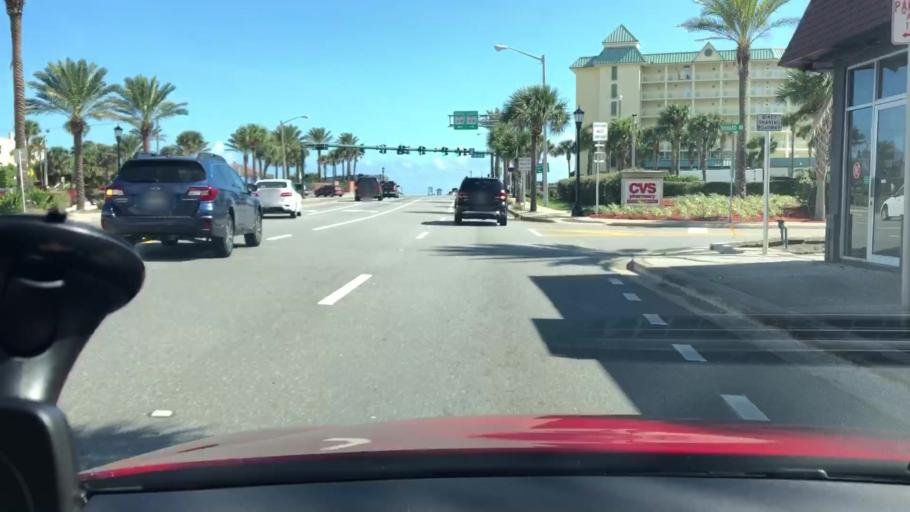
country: US
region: Florida
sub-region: Volusia County
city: Ormond Beach
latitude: 29.2915
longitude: -81.0408
